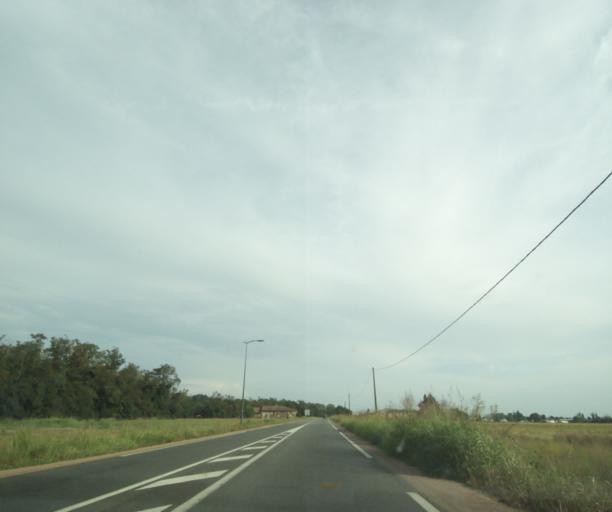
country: FR
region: Midi-Pyrenees
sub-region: Departement du Tarn-et-Garonne
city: Grisolles
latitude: 43.8454
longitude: 1.2875
